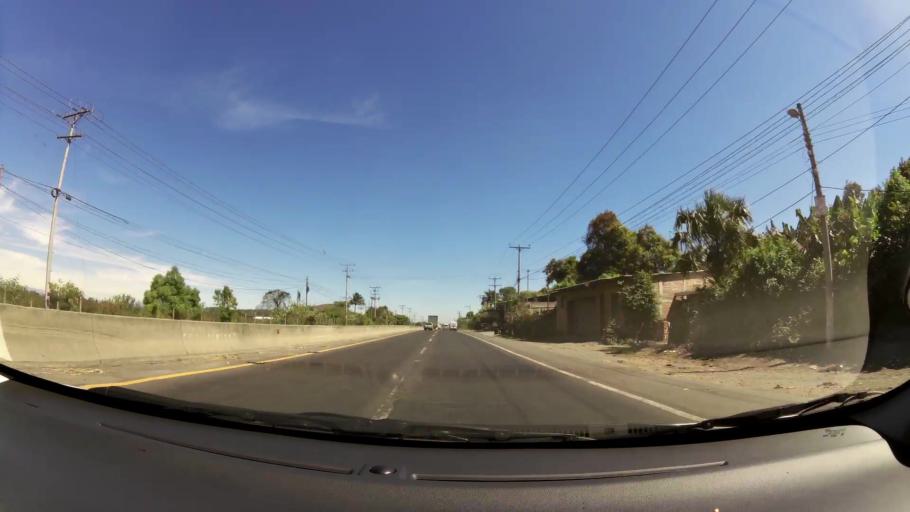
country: SV
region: La Libertad
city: San Juan Opico
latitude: 13.7887
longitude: -89.3569
